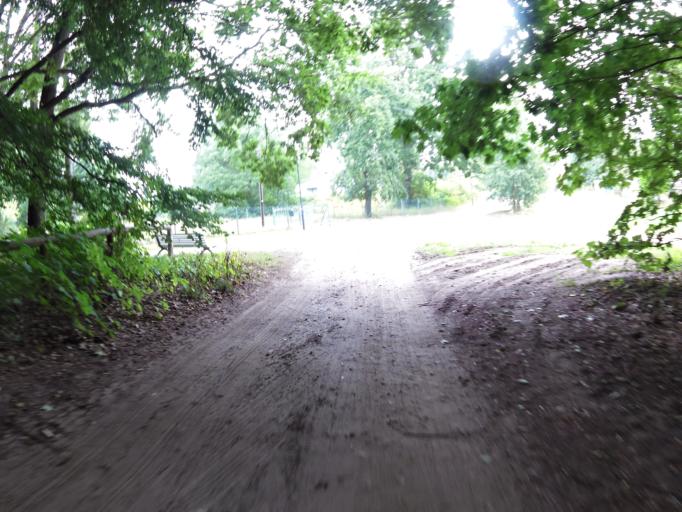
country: DE
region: Mecklenburg-Vorpommern
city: Seebad Heringsdorf
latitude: 53.9322
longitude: 14.1818
